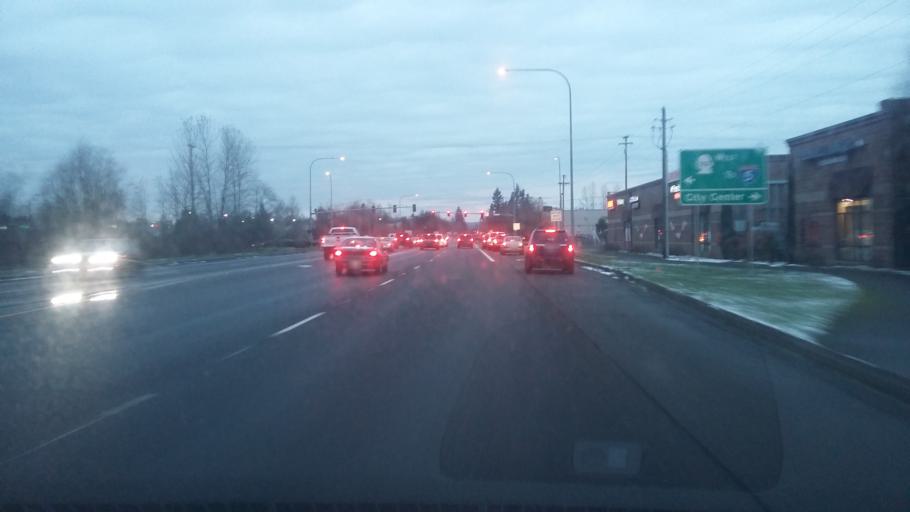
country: US
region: Washington
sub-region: Clark County
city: Battle Ground
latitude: 45.7792
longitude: -122.5475
